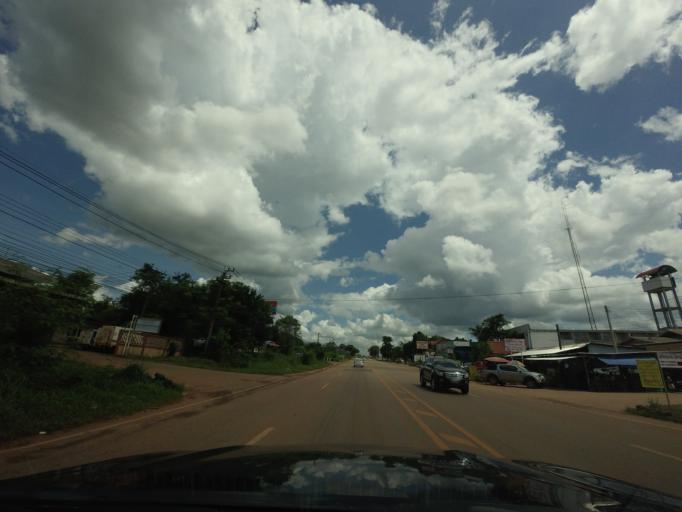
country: TH
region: Changwat Udon Thani
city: Ban Dung
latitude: 17.6772
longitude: 103.2480
